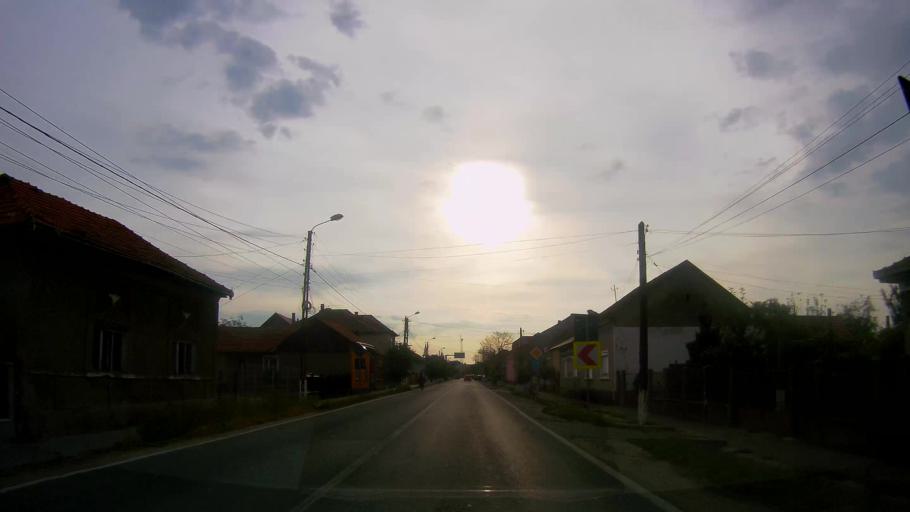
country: RO
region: Satu Mare
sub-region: Comuna Halmeu
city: Halmeu
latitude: 47.9776
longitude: 23.0106
